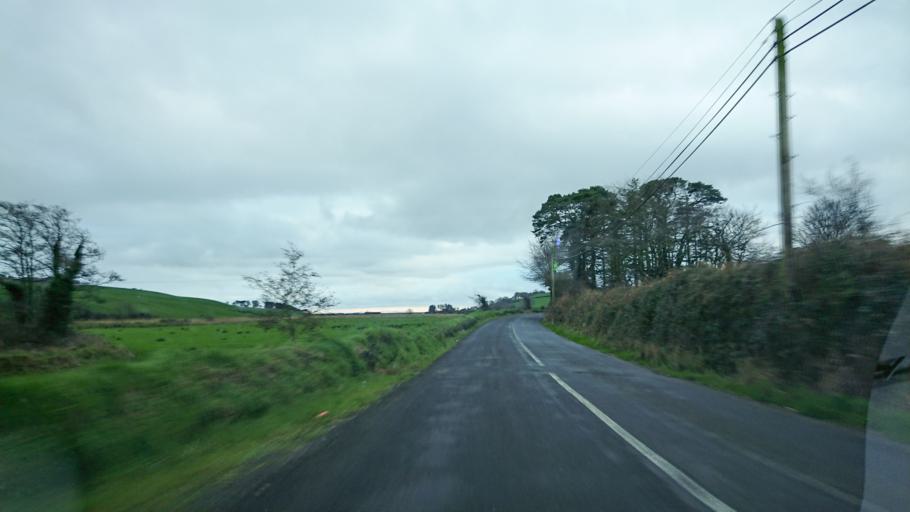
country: IE
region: Munster
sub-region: Waterford
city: Portlaw
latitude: 52.1517
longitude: -7.3800
